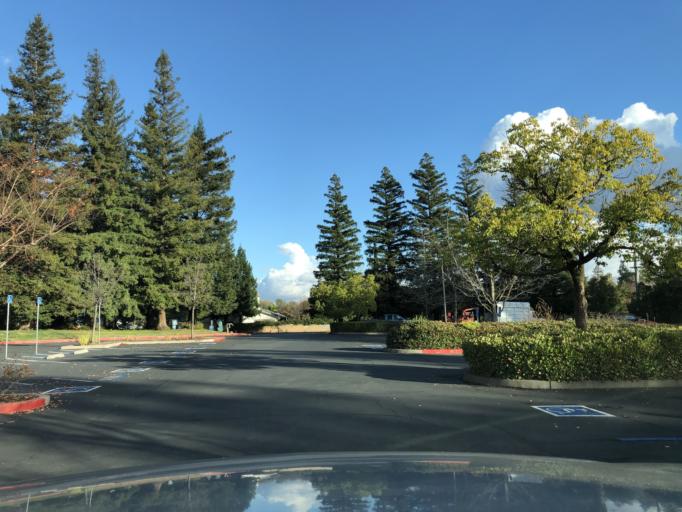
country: US
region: California
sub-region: Sacramento County
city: Foothill Farms
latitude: 38.6575
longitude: -121.3286
